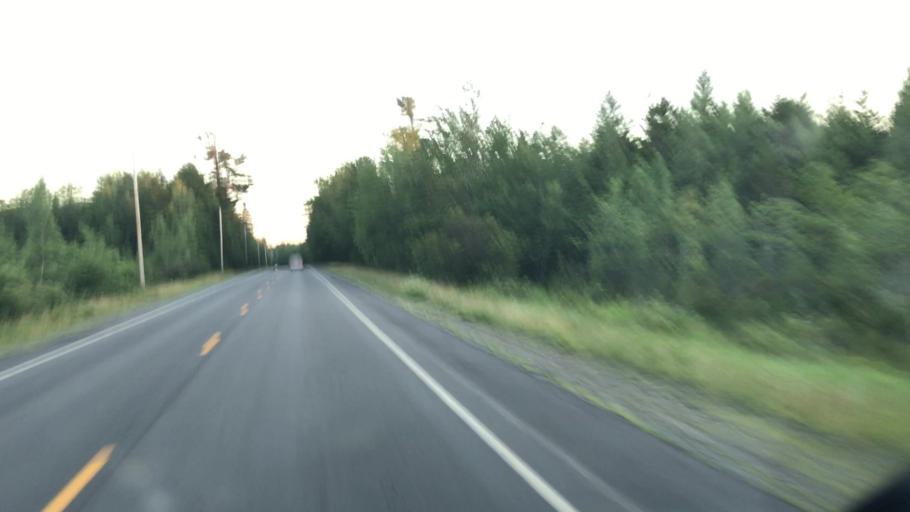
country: US
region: Maine
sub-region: Penobscot County
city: Medway
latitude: 45.5812
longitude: -68.3175
